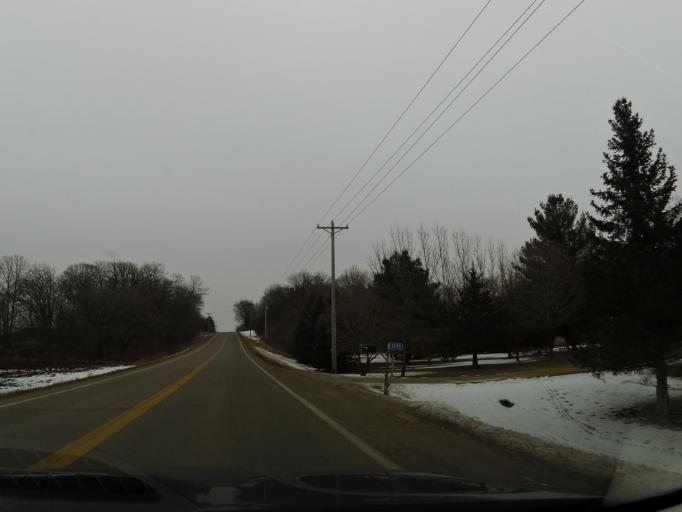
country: US
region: Minnesota
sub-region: Scott County
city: Jordan
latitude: 44.6306
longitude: -93.5875
